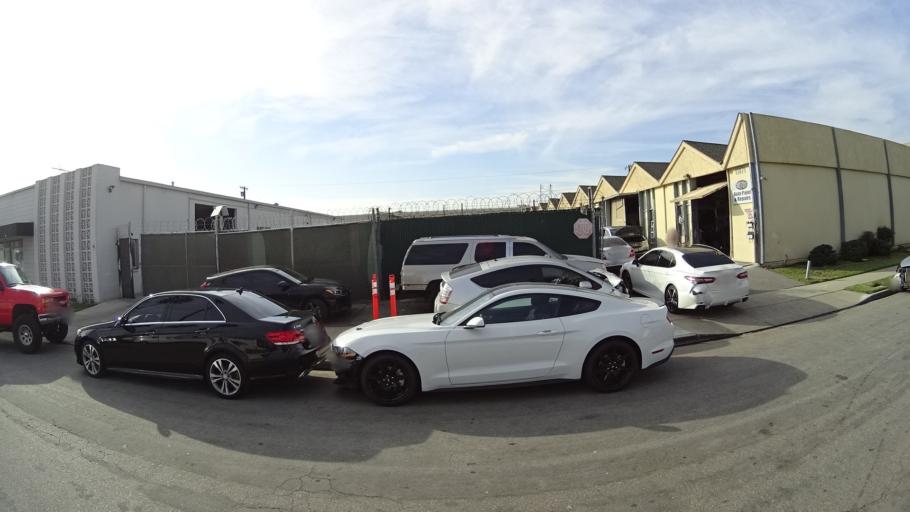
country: US
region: California
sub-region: Orange County
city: Garden Grove
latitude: 33.7613
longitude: -117.9238
